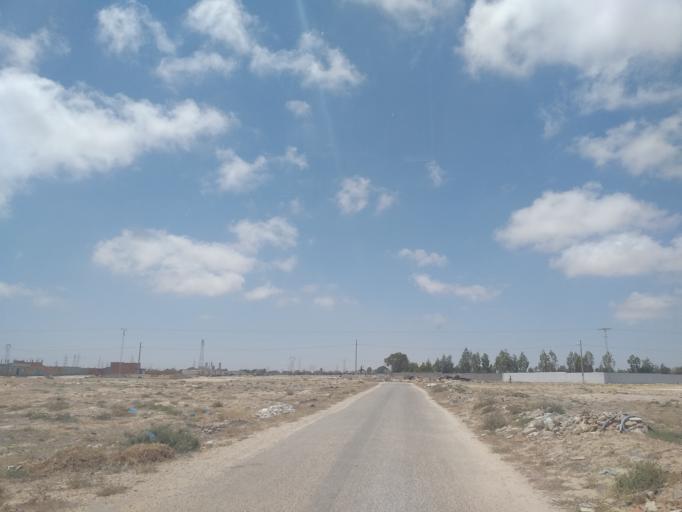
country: TN
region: Qabis
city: Gabes
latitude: 33.9287
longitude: 10.0484
